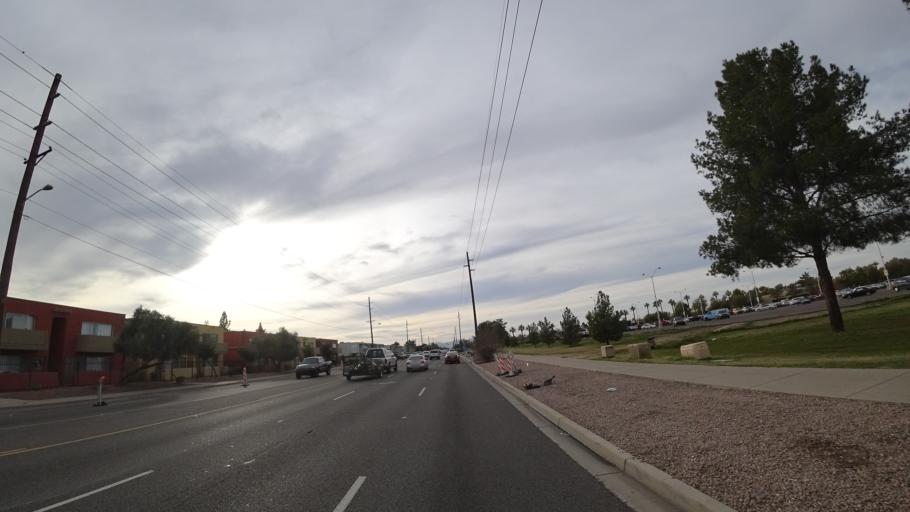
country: US
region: Arizona
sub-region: Maricopa County
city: Glendale
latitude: 33.5676
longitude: -112.1874
